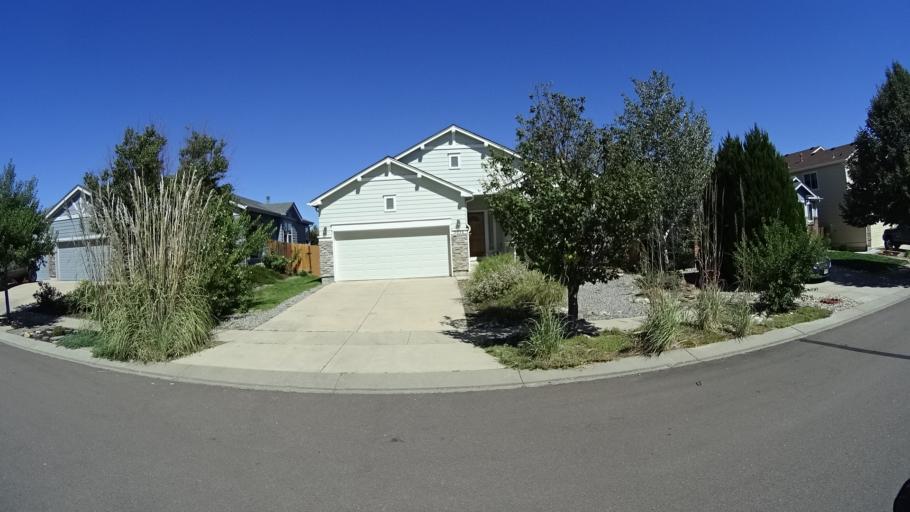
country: US
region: Colorado
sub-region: El Paso County
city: Security-Widefield
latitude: 38.7843
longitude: -104.7286
